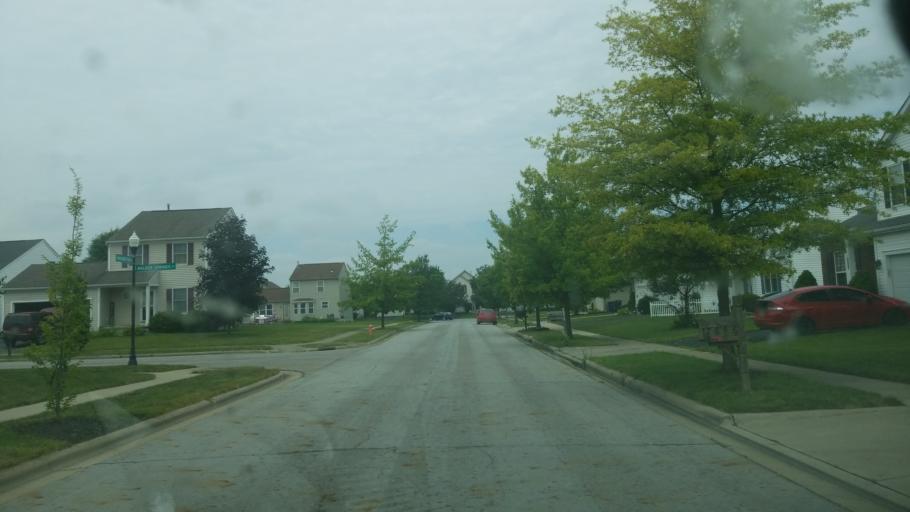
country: US
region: Ohio
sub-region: Franklin County
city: Reynoldsburg
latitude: 40.0092
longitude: -82.7841
